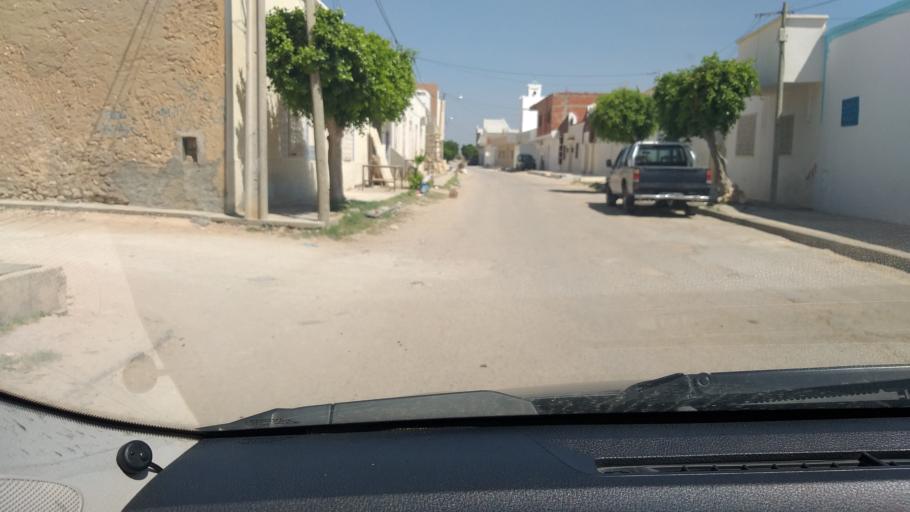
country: TN
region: Al Mahdiyah
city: El Jem
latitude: 35.2917
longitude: 10.7154
